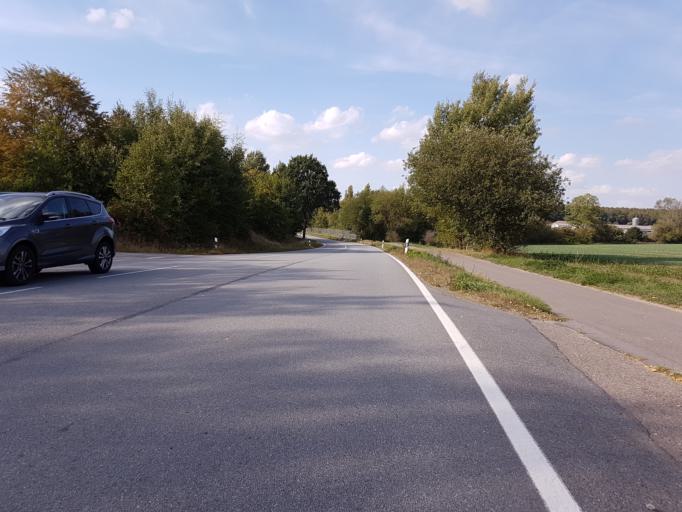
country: DE
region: Saxony
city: Claussnitz
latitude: 50.9418
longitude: 12.8757
